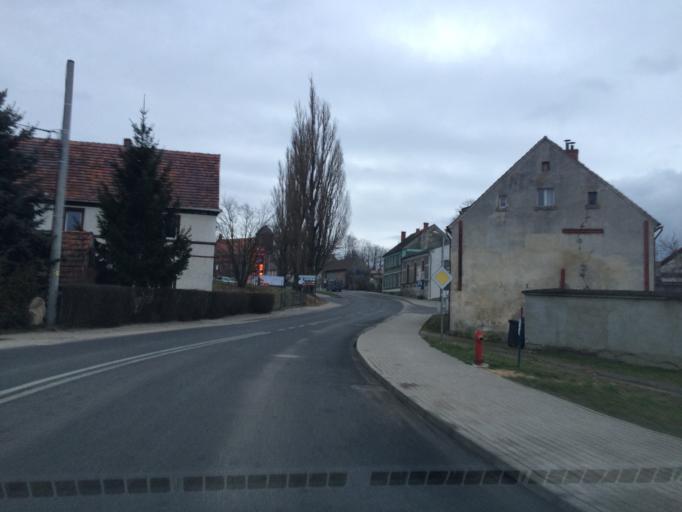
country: PL
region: Lower Silesian Voivodeship
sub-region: Powiat boleslawiecki
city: Nowogrodziec
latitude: 51.1959
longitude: 15.3902
